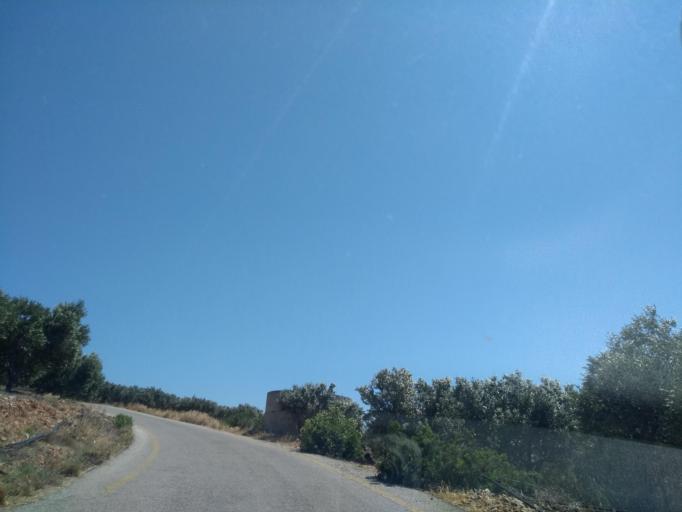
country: GR
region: Crete
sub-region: Nomos Chanias
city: Vryses
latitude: 35.3596
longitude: 23.5422
